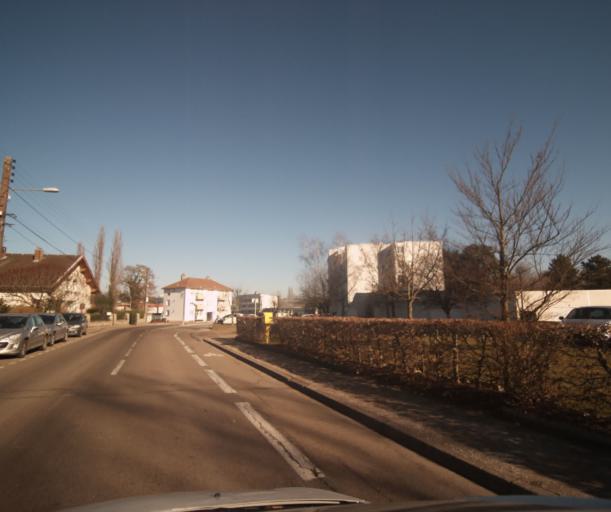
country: FR
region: Franche-Comte
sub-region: Departement du Doubs
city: Besancon
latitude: 47.2342
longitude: 5.9938
